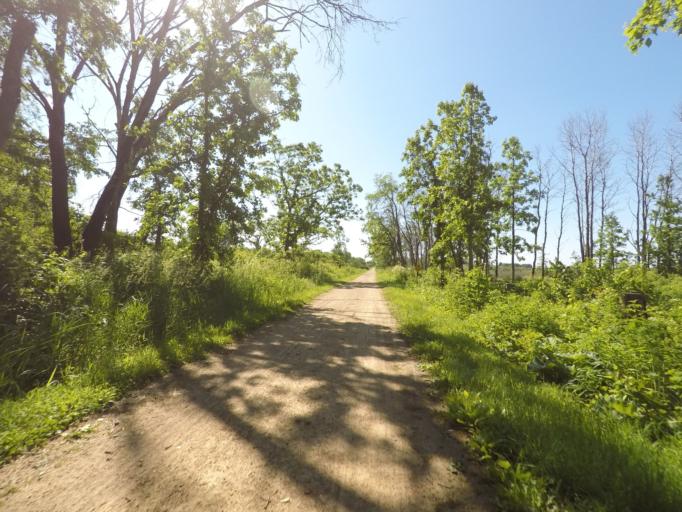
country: US
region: Wisconsin
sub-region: Dane County
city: Verona
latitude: 42.9849
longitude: -89.5654
